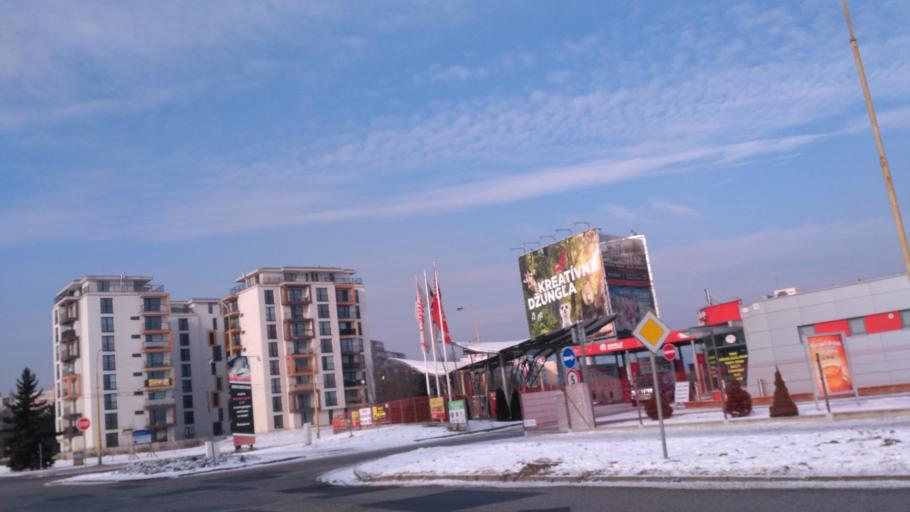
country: SK
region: Kosicky
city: Kosice
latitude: 48.7091
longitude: 21.2473
